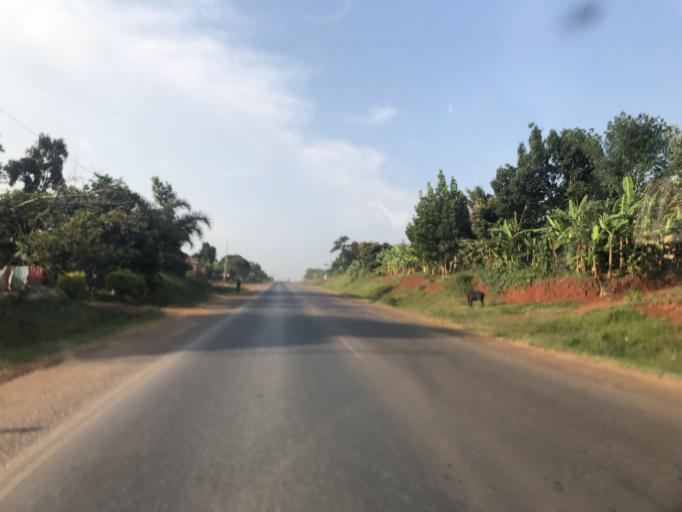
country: UG
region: Central Region
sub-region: Butambala District
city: Gombe
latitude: 0.1126
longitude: 32.1779
